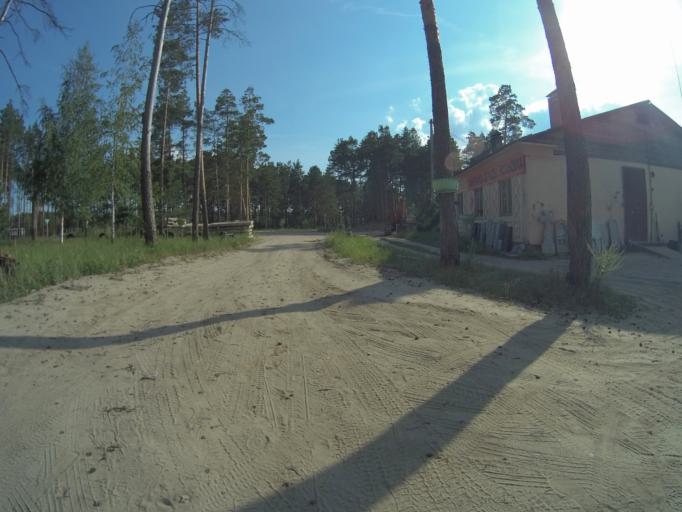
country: RU
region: Vladimir
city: Golovino
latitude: 56.0375
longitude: 40.4240
